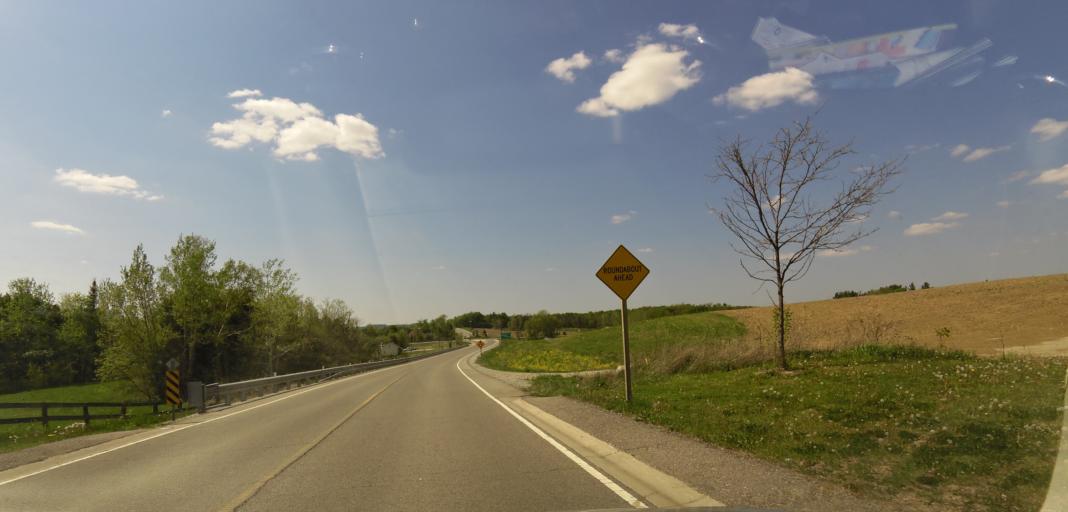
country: CA
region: Ontario
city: Brampton
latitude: 43.8278
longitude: -79.8807
